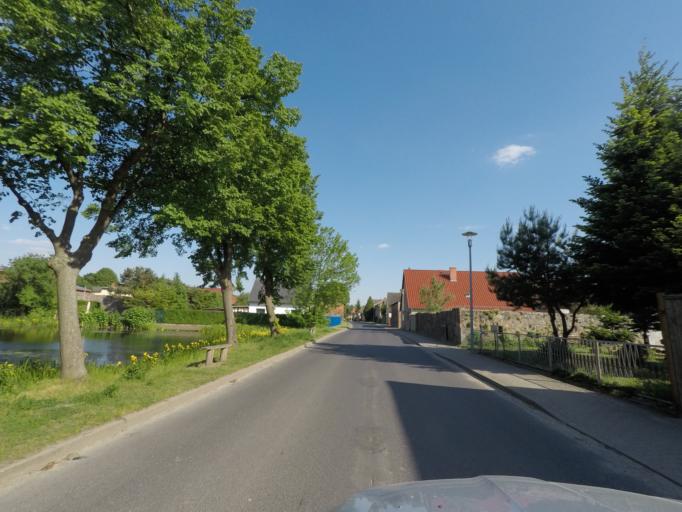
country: DE
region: Brandenburg
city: Werftpfuhl
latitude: 52.7387
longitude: 13.8354
